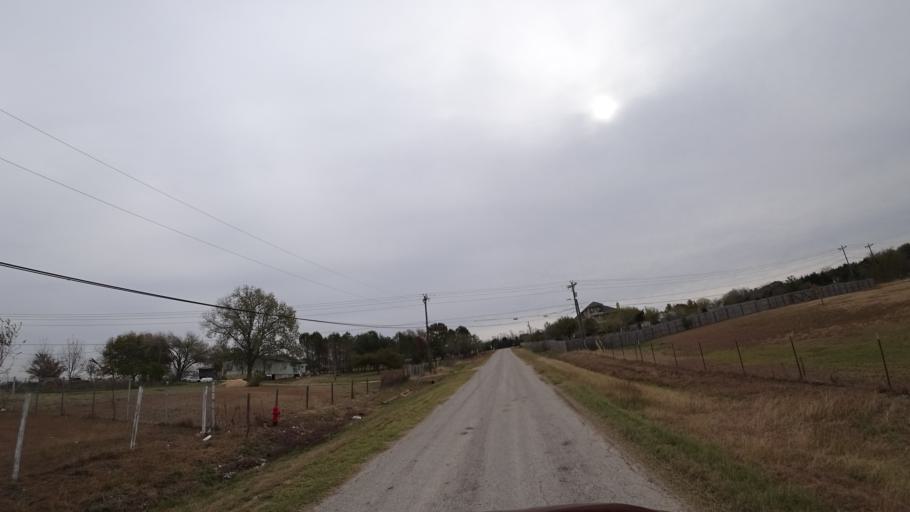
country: US
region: Texas
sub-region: Travis County
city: Garfield
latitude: 30.1167
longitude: -97.5810
